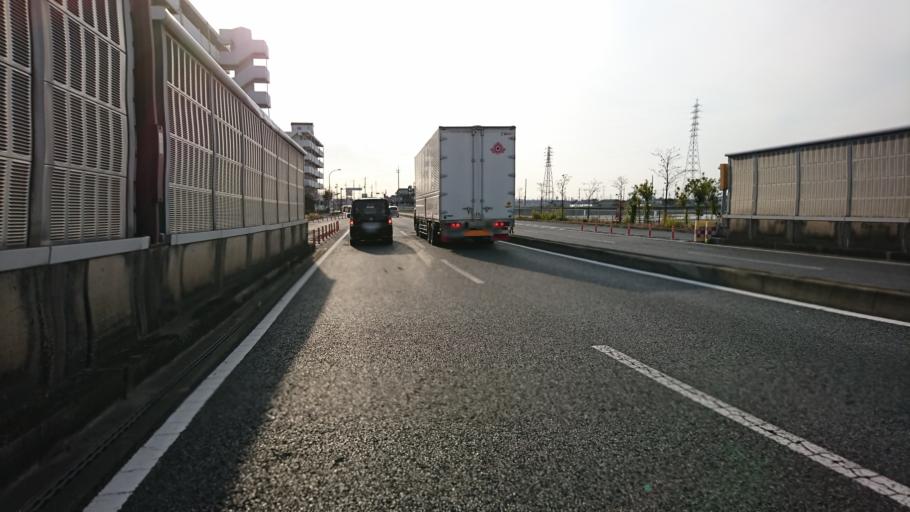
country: JP
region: Hyogo
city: Kakogawacho-honmachi
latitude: 34.7149
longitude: 134.8877
